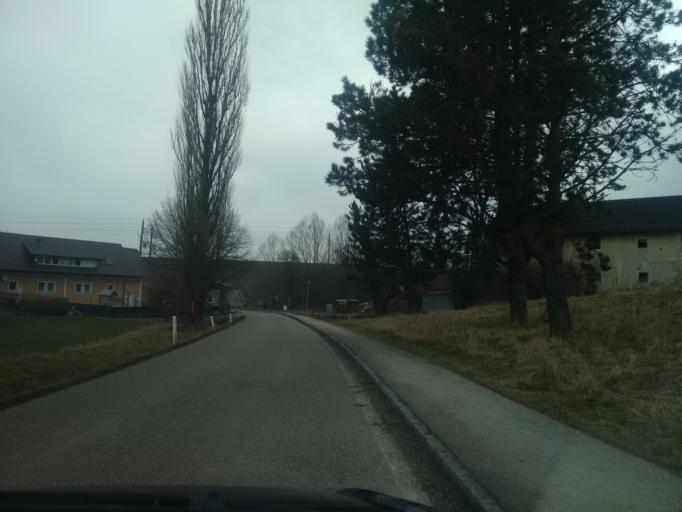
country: AT
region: Upper Austria
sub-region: Wels-Land
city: Buchkirchen
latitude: 48.1949
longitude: 13.9756
